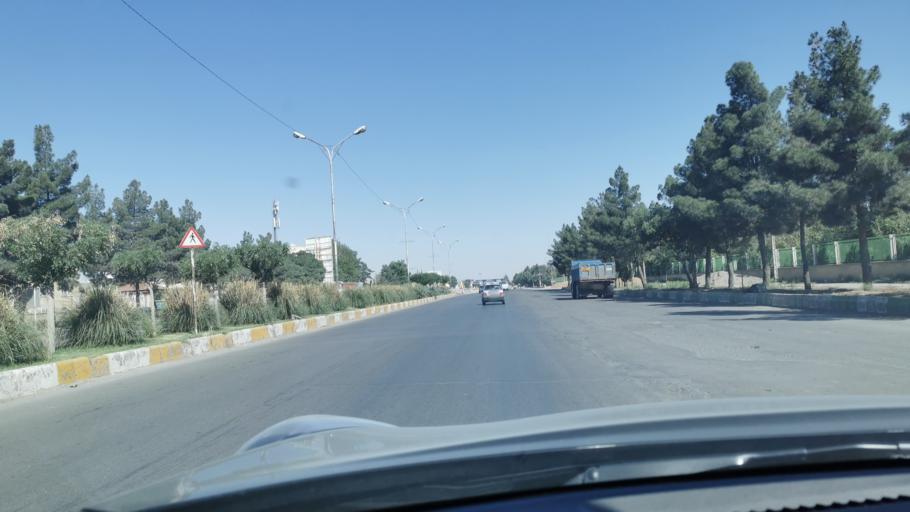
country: IR
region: Razavi Khorasan
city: Chenaran
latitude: 36.6384
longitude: 59.1225
